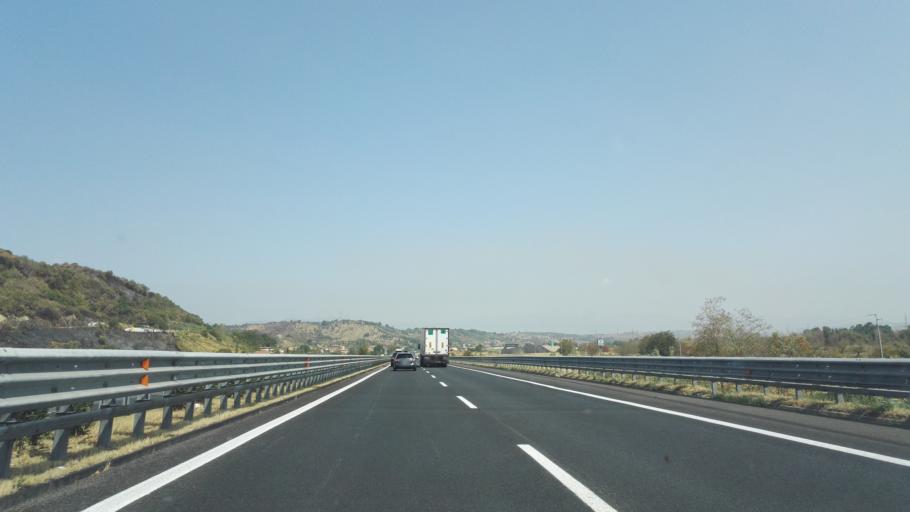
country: IT
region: Calabria
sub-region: Provincia di Cosenza
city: Sartano
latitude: 39.4838
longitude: 16.2141
